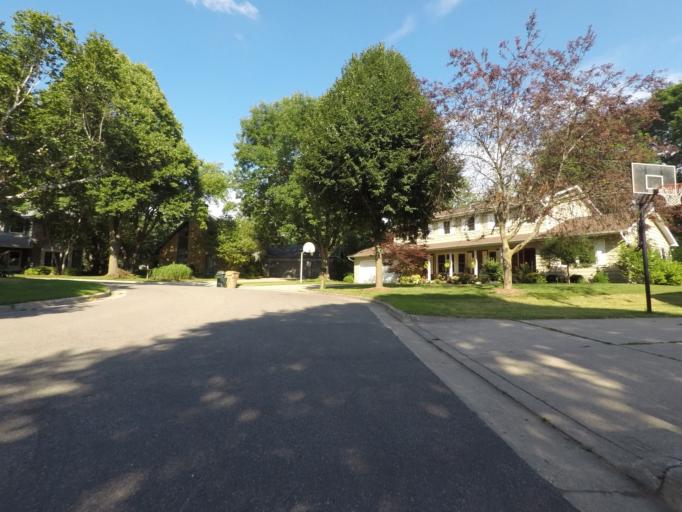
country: US
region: Wisconsin
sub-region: Dane County
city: Middleton
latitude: 43.0719
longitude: -89.5050
